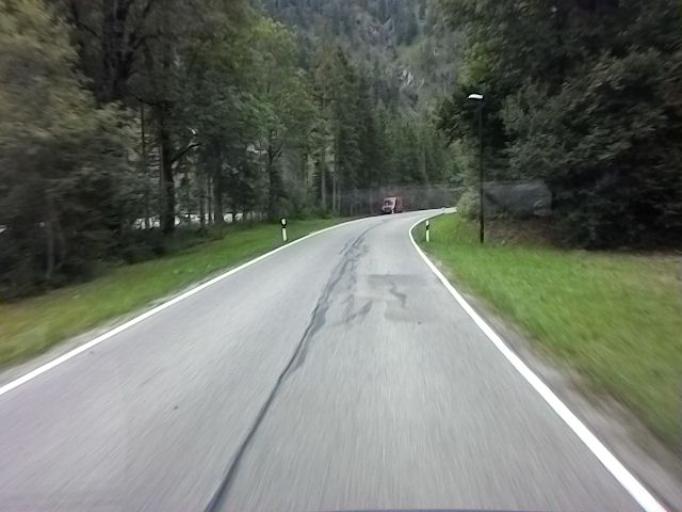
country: DE
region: Bavaria
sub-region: Upper Bavaria
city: Jachenau
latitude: 47.5566
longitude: 11.4349
